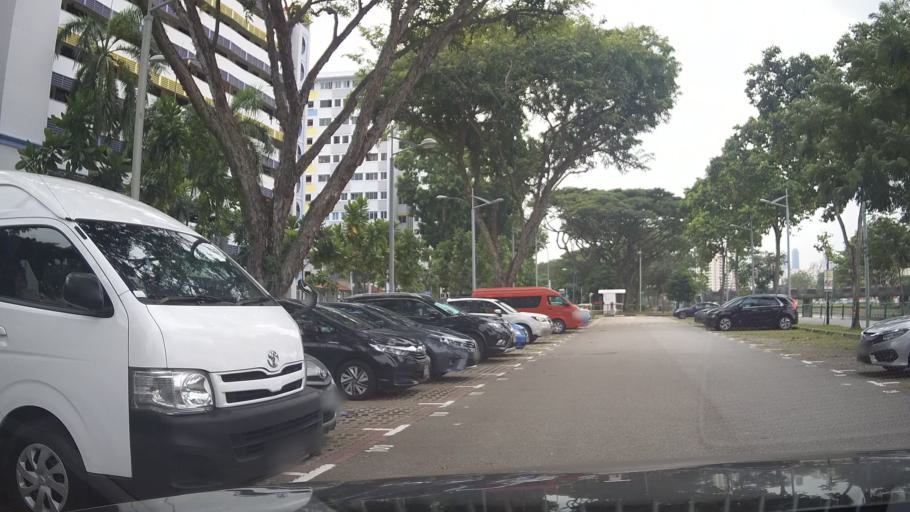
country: SG
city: Singapore
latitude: 1.3033
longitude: 103.8830
